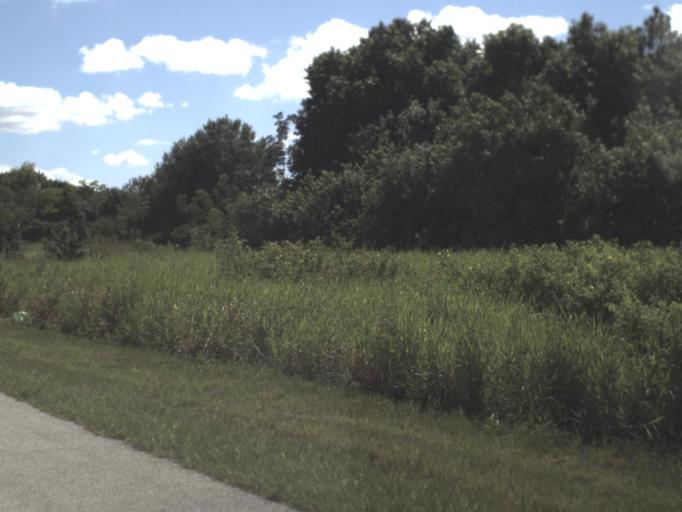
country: US
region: Florida
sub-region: Collier County
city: Lely Resort
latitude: 26.0194
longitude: -81.6306
